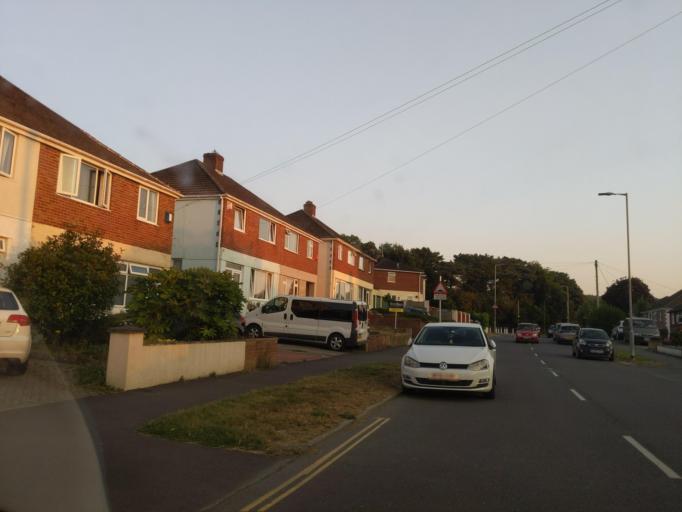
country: GB
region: England
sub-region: Devon
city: Plympton
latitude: 50.3949
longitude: -4.0689
